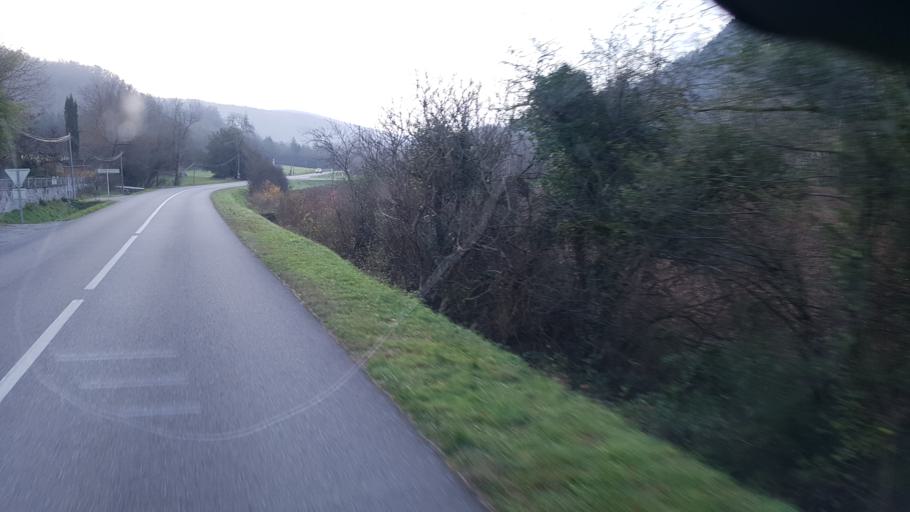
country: FR
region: Midi-Pyrenees
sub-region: Departement du Tarn-et-Garonne
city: Montricoux
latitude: 44.0555
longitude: 1.6712
